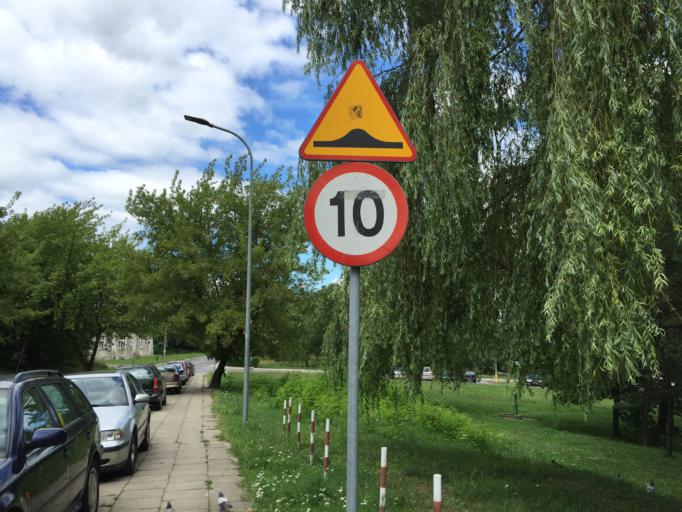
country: PL
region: Lesser Poland Voivodeship
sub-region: Krakow
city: Krakow
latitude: 50.0326
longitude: 19.9677
